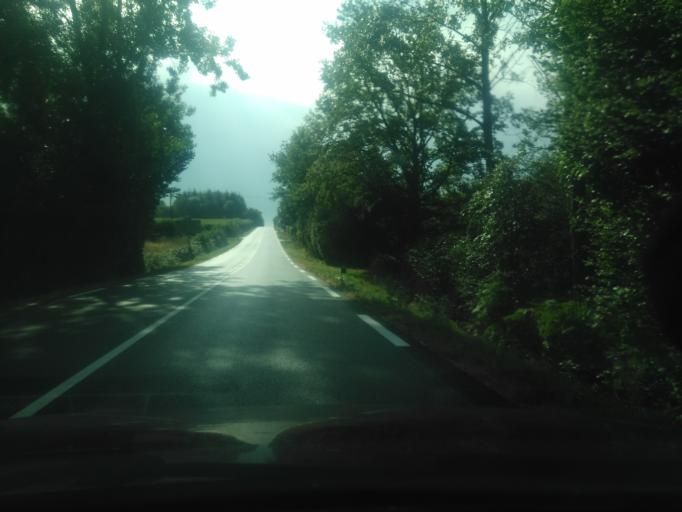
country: FR
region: Poitou-Charentes
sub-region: Departement des Deux-Sevres
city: Secondigny
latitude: 46.6122
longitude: -0.4348
